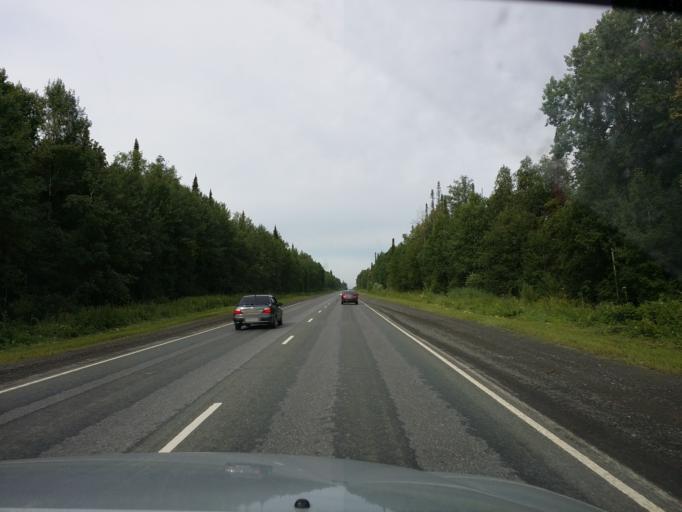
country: RU
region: Tjumen
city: Abalak
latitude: 58.4727
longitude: 68.5854
